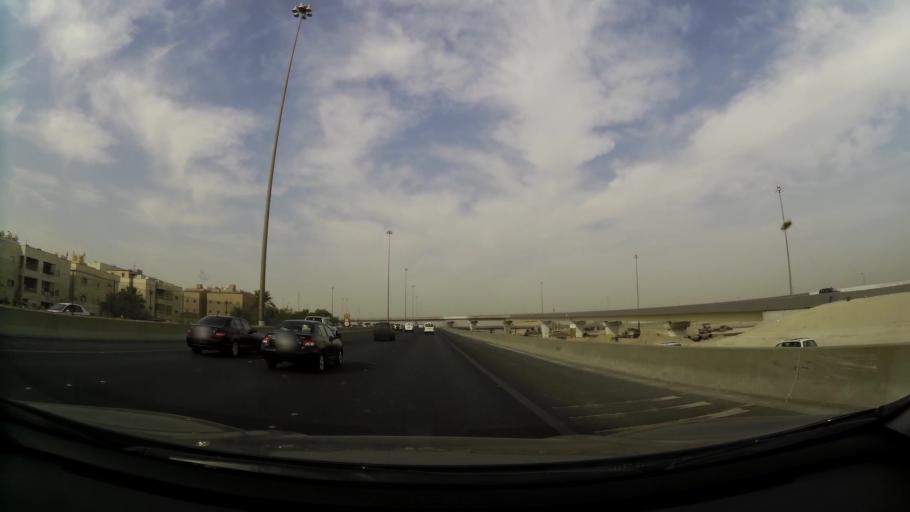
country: KW
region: Al Asimah
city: Ar Rabiyah
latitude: 29.2674
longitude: 47.9128
